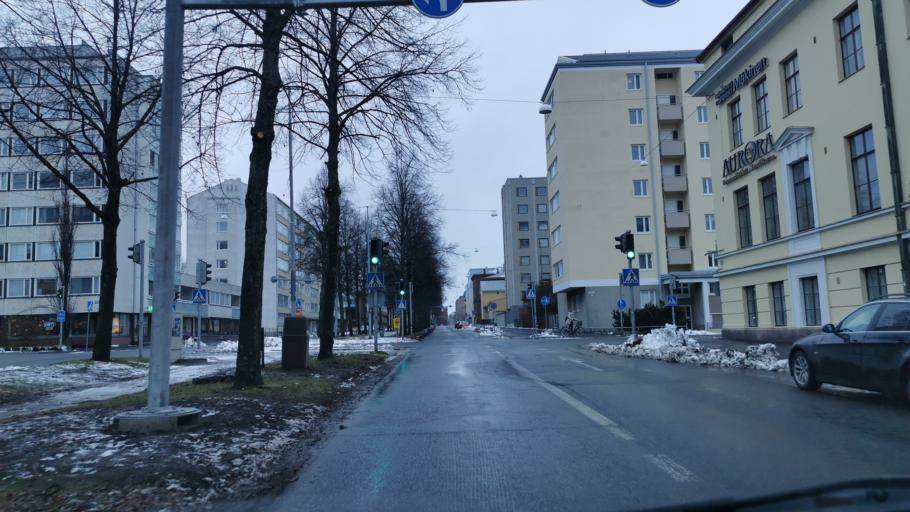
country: FI
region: Ostrobothnia
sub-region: Vaasa
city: Vaasa
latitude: 63.1001
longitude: 21.6053
